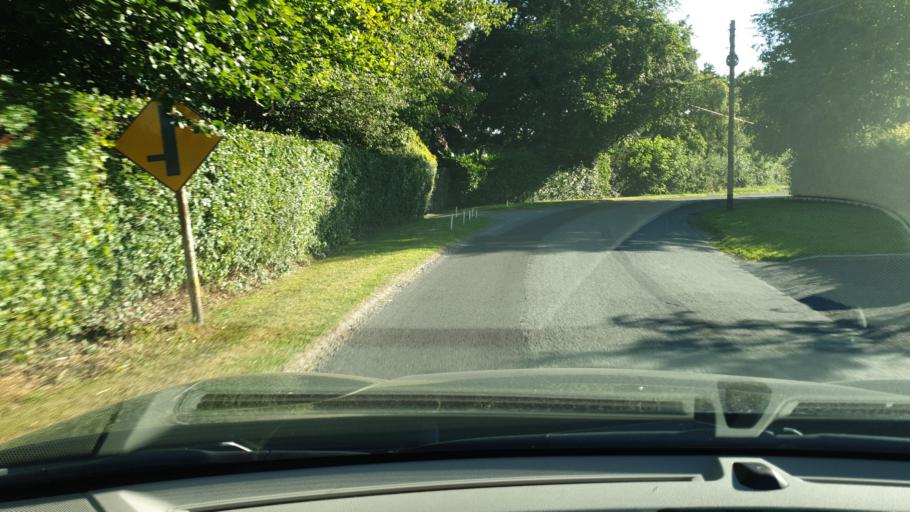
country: IE
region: Leinster
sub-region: An Mhi
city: Ashbourne
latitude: 53.4593
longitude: -6.3843
